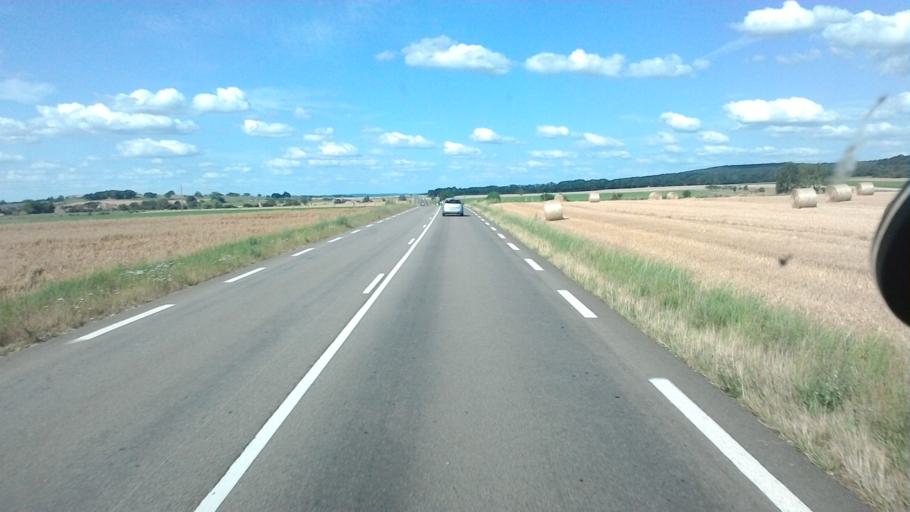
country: FR
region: Franche-Comte
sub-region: Departement de la Haute-Saone
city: Gy
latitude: 47.4497
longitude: 5.8916
